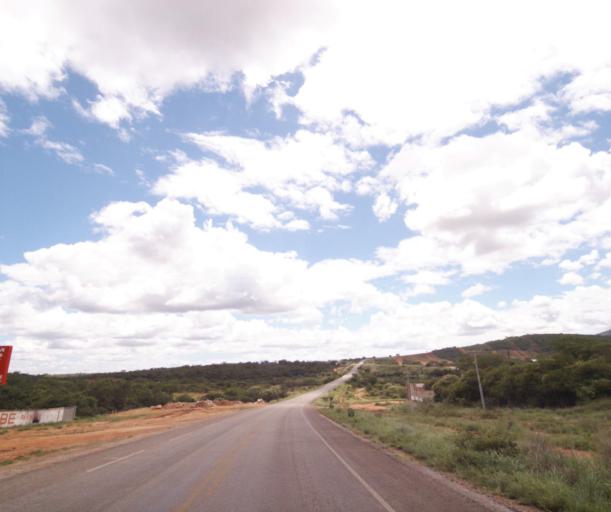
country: BR
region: Bahia
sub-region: Brumado
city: Brumado
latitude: -14.2299
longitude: -41.6784
